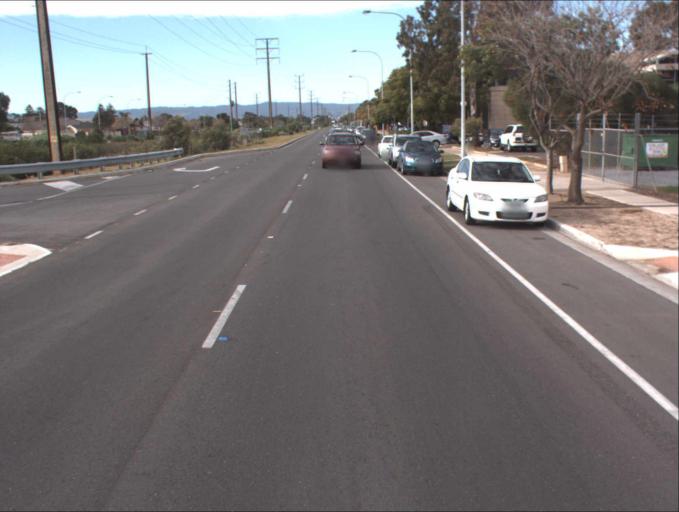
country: AU
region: South Australia
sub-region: Port Adelaide Enfield
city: Cheltenham
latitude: -34.8610
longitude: 138.5051
